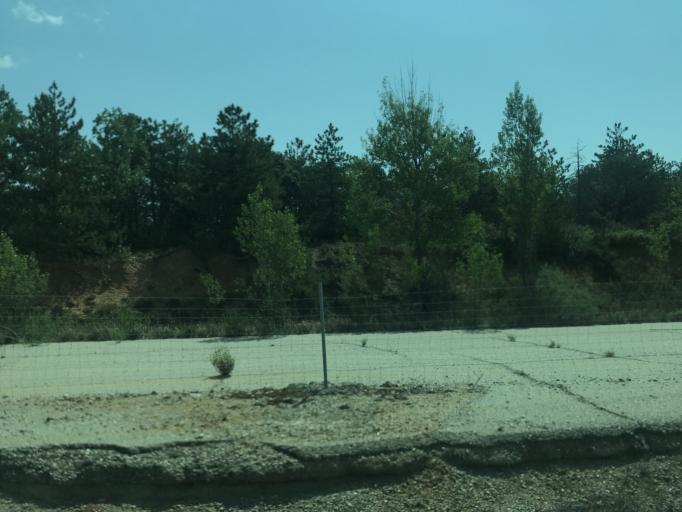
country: ES
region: Castille and Leon
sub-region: Provincia de Segovia
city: Castillejo de Mesleon
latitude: 41.2969
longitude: -3.6035
